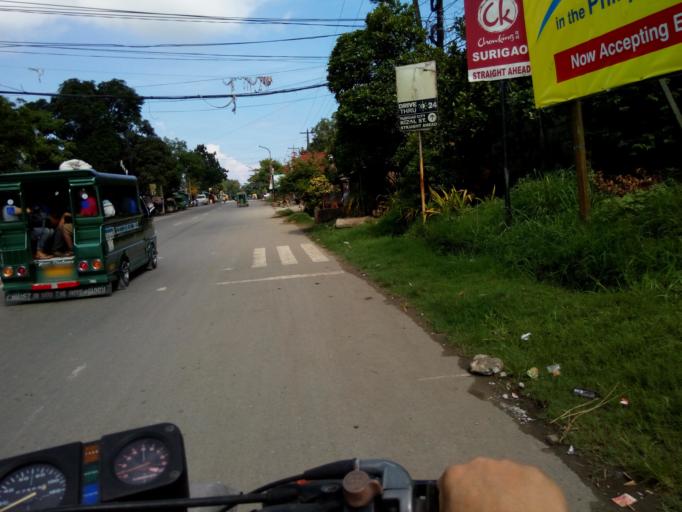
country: PH
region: Caraga
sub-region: Province of Surigao del Norte
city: Surigao
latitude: 9.7759
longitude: 125.4833
